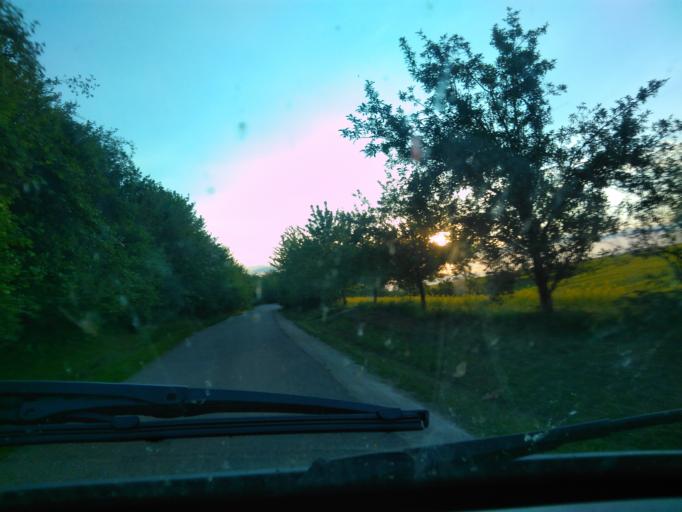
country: DE
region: Saxony-Anhalt
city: Mertendorf
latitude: 51.1164
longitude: 11.8328
